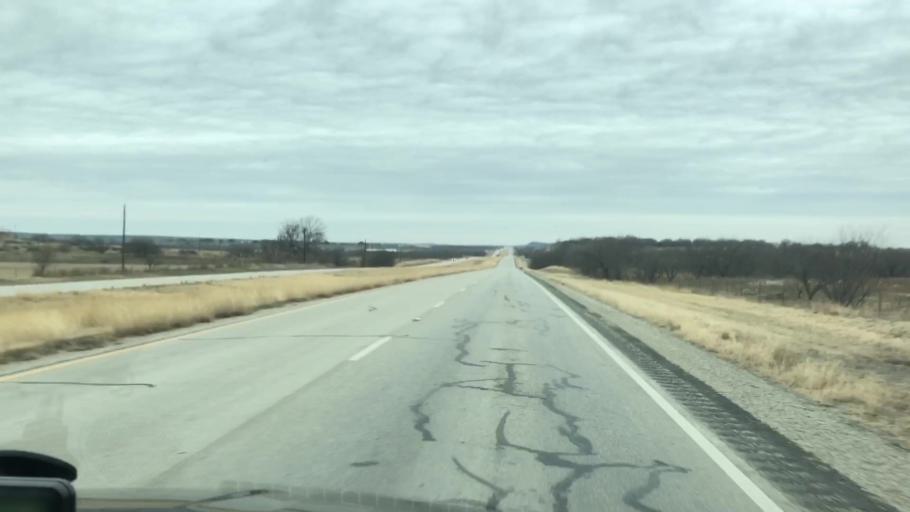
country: US
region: Texas
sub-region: Jack County
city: Jacksboro
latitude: 33.2355
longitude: -98.2051
